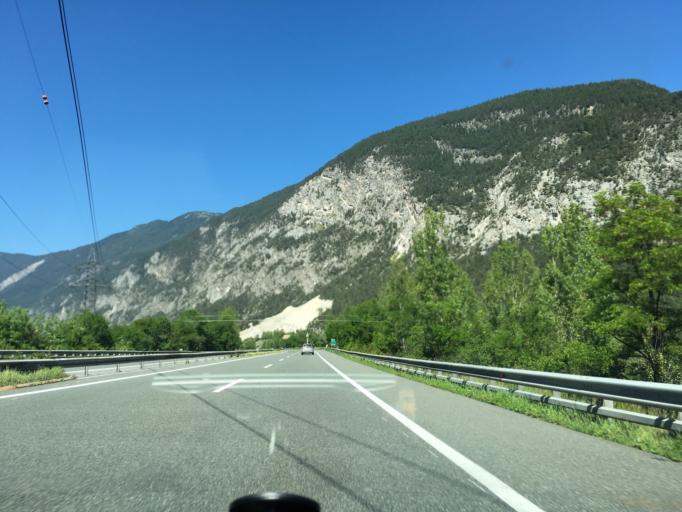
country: AT
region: Tyrol
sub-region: Politischer Bezirk Imst
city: Motz
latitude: 47.2726
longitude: 10.9475
